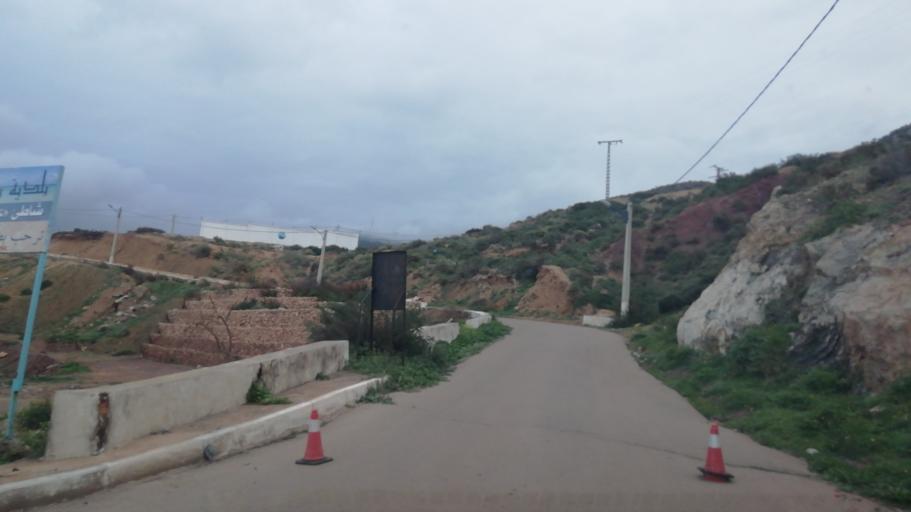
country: DZ
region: Oran
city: Bir el Djir
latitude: 35.7676
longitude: -0.5281
